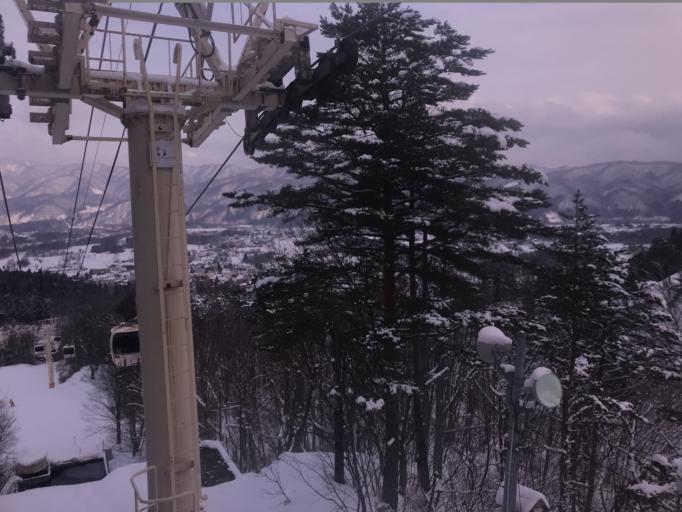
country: JP
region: Nagano
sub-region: Kitaazumi Gun
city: Hakuba
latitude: 36.7009
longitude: 137.8326
